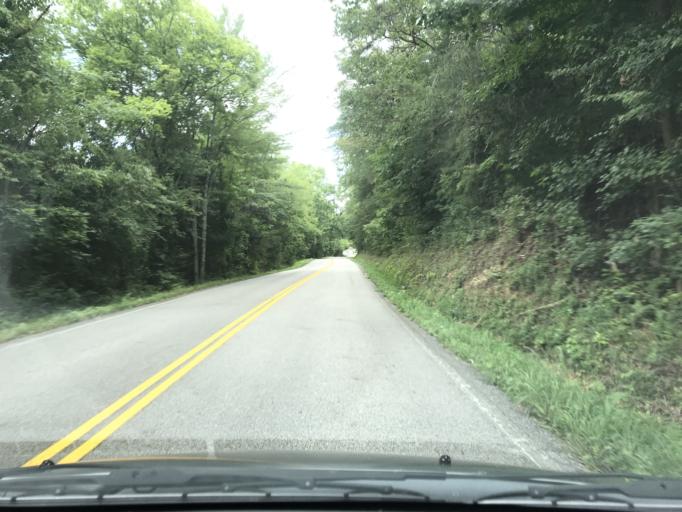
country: US
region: Tennessee
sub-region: Hamilton County
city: Lakesite
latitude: 35.1704
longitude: -85.0852
